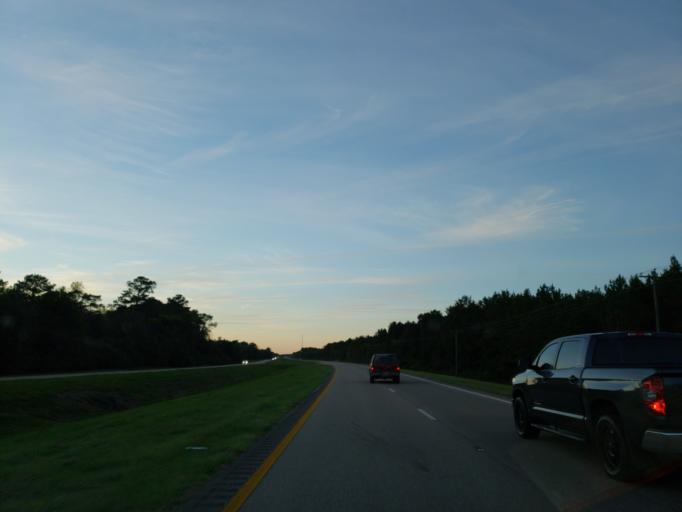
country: US
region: Mississippi
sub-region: Wayne County
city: Belmont
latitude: 31.6014
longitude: -88.5576
